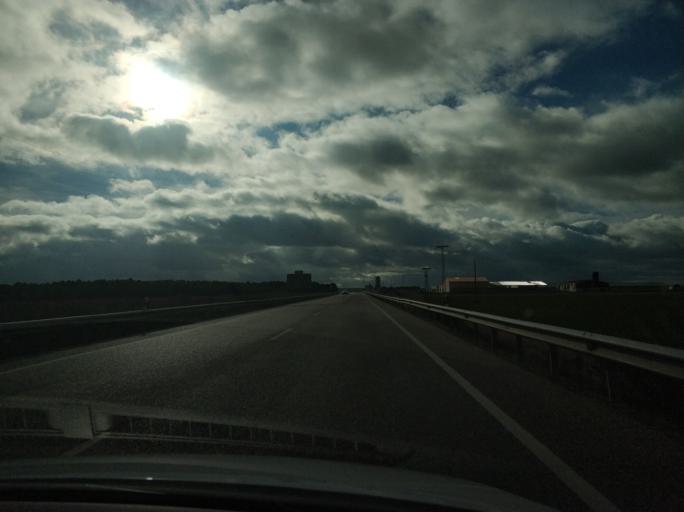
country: ES
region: Castille and Leon
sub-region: Provincia de Segovia
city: Ayllon
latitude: 41.4106
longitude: -3.4125
